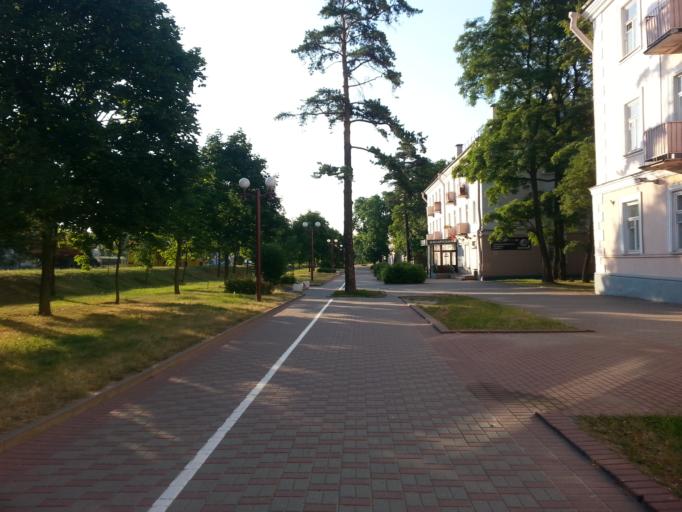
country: BY
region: Minsk
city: Vyaliki Trastsyanets
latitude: 53.8676
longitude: 27.6527
